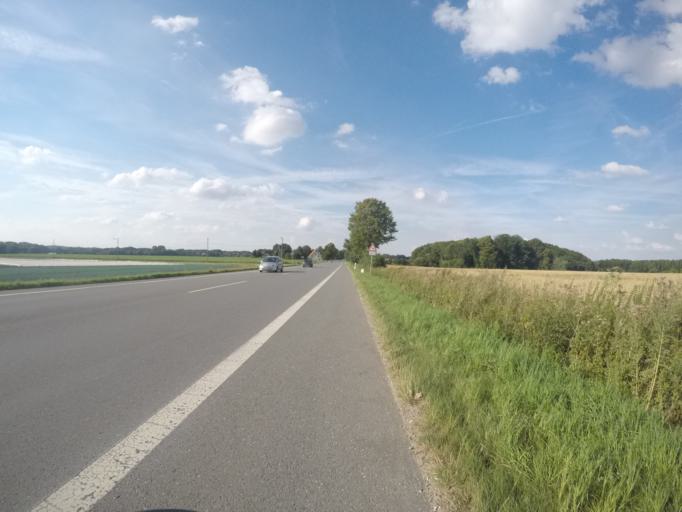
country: DE
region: North Rhine-Westphalia
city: Enger
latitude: 52.0811
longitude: 8.5846
